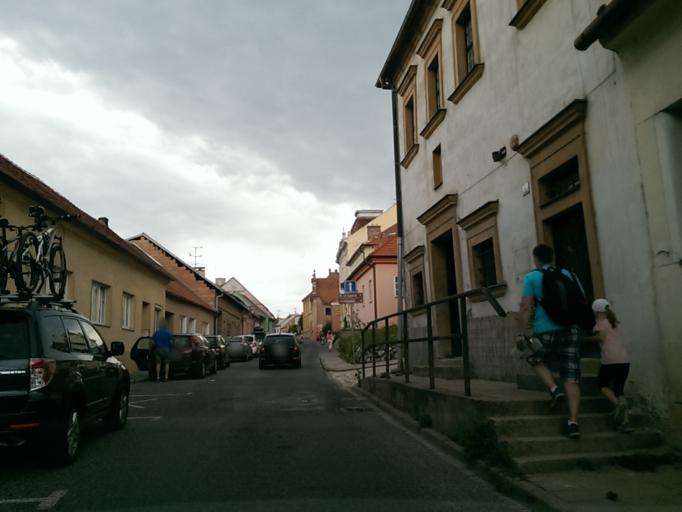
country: CZ
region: South Moravian
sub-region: Okres Breclav
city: Mikulov
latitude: 48.8049
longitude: 16.6403
